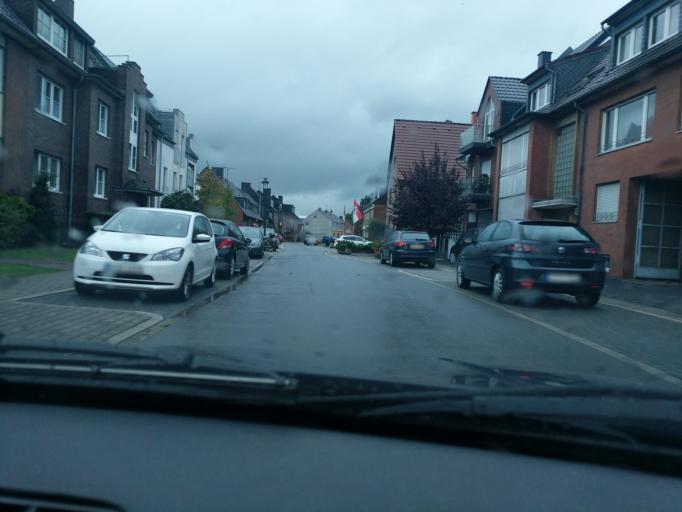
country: DE
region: North Rhine-Westphalia
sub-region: Regierungsbezirk Dusseldorf
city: Dusseldorf
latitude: 51.2010
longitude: 6.7386
